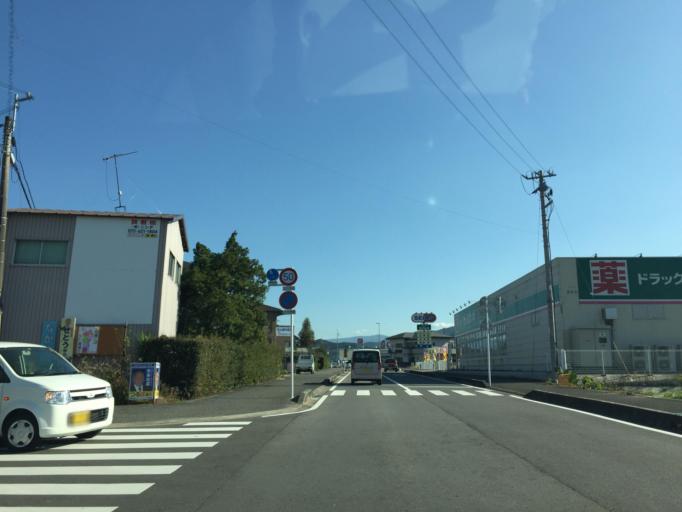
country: JP
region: Wakayama
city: Kainan
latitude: 34.1627
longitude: 135.2797
